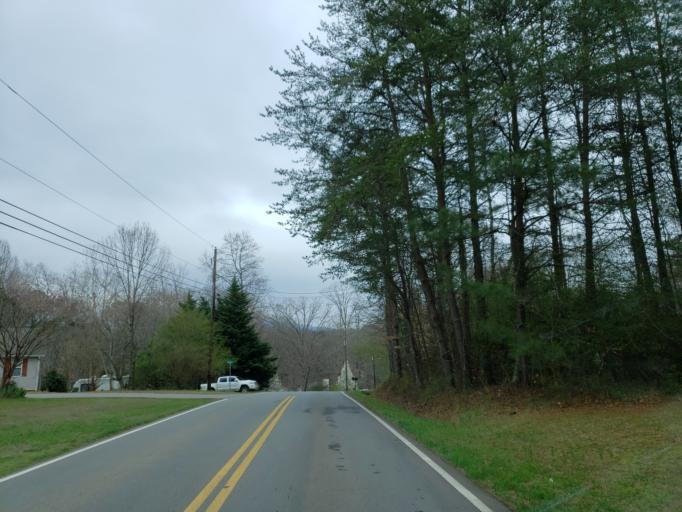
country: US
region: Georgia
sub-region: Pickens County
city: Jasper
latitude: 34.4767
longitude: -84.4360
